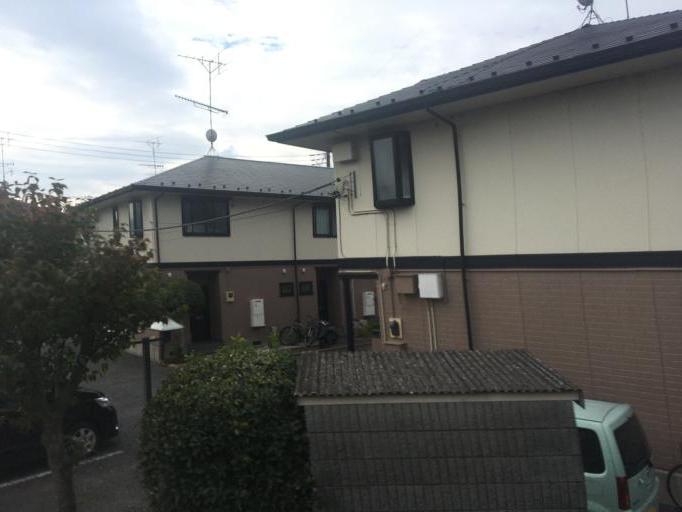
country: JP
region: Tokyo
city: Fussa
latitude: 35.7055
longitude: 139.3591
